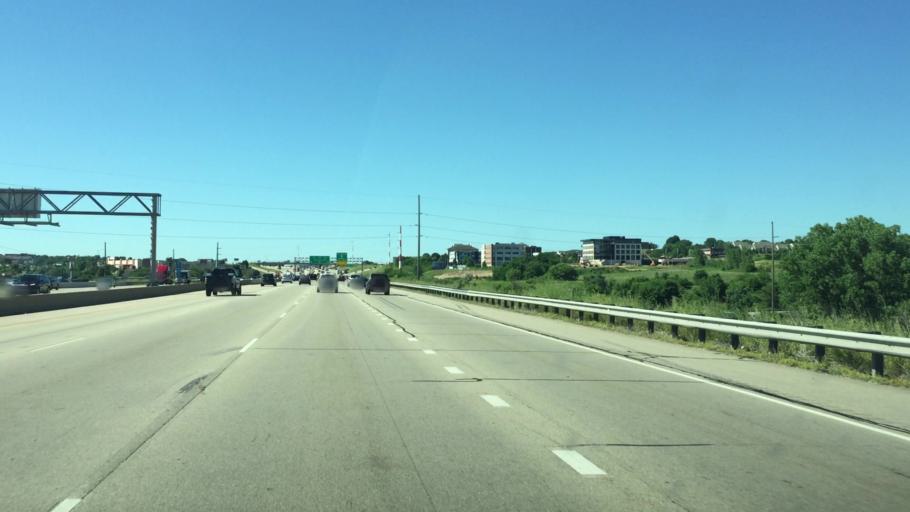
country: US
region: Wisconsin
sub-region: Dane County
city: Monona
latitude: 43.1235
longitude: -89.2898
